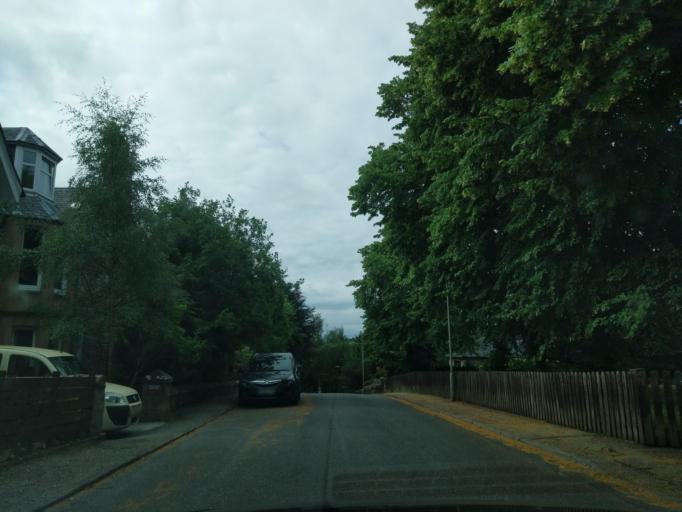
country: GB
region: Scotland
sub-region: Highland
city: Grantown on Spey
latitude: 57.3260
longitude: -3.6110
